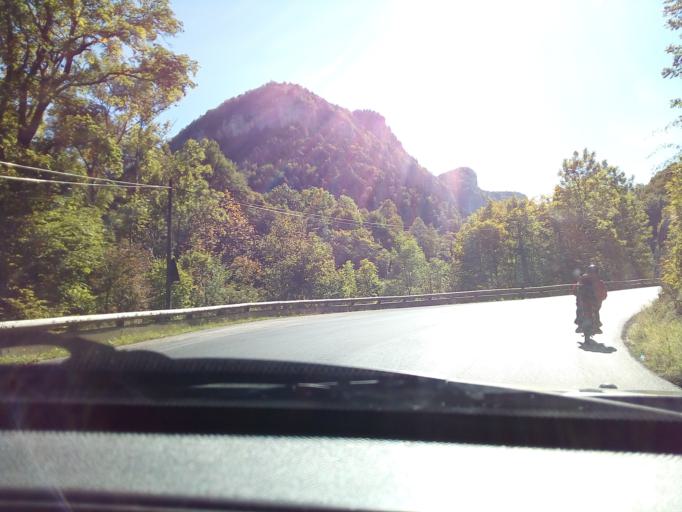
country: FR
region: Rhone-Alpes
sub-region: Departement de l'Isere
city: Sassenage
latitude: 45.1855
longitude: 5.6218
